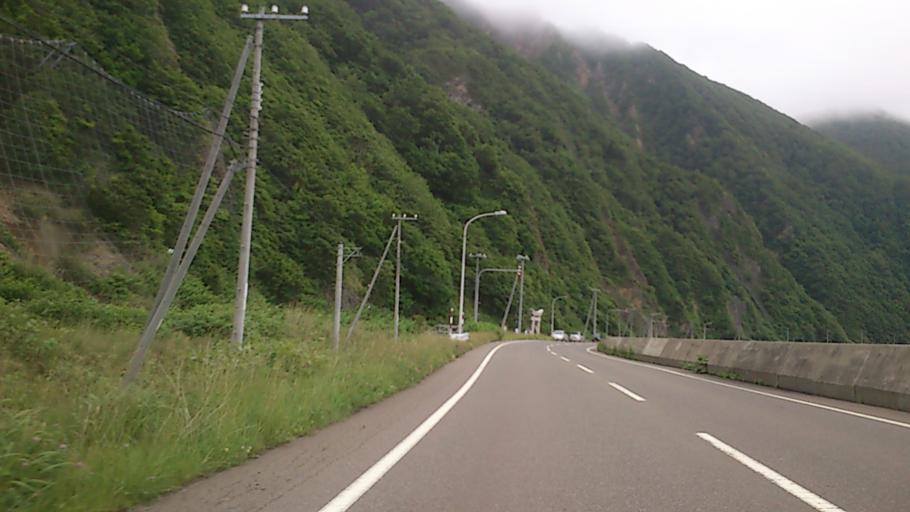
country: JP
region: Hokkaido
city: Kamiiso
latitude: 42.2727
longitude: 139.7853
